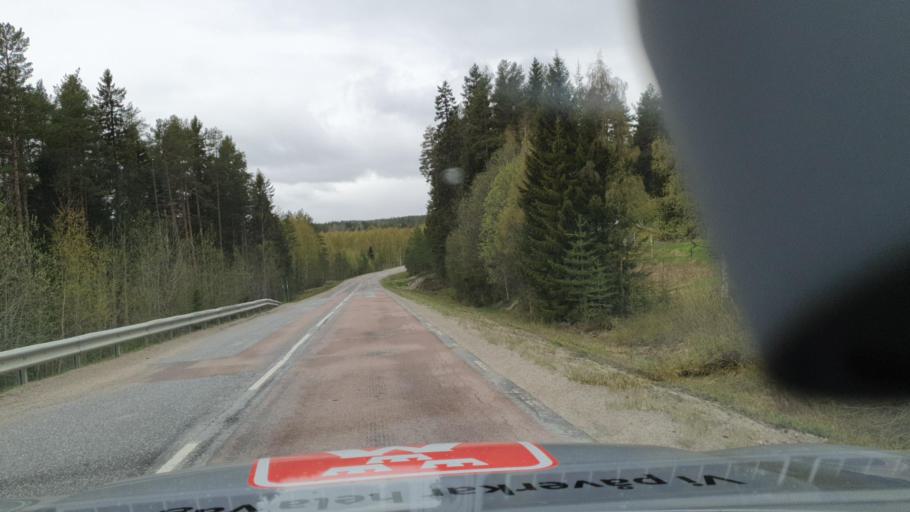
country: SE
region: Vaesternorrland
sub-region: OErnskoeldsviks Kommun
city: Bredbyn
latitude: 63.5750
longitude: 17.6039
